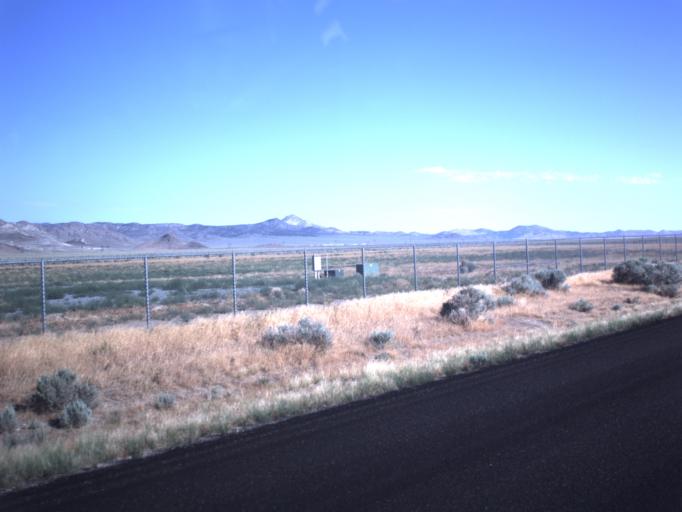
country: US
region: Utah
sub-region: Beaver County
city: Milford
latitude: 38.4372
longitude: -113.0097
